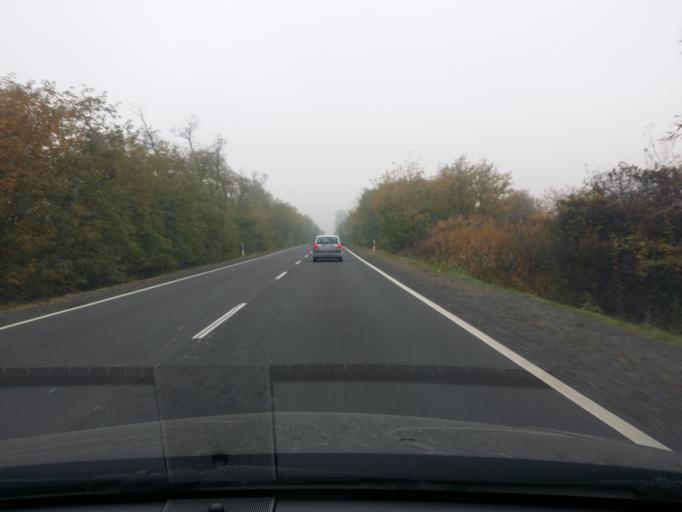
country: HU
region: Szabolcs-Szatmar-Bereg
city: Nyirbogdany
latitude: 48.0267
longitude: 21.8484
